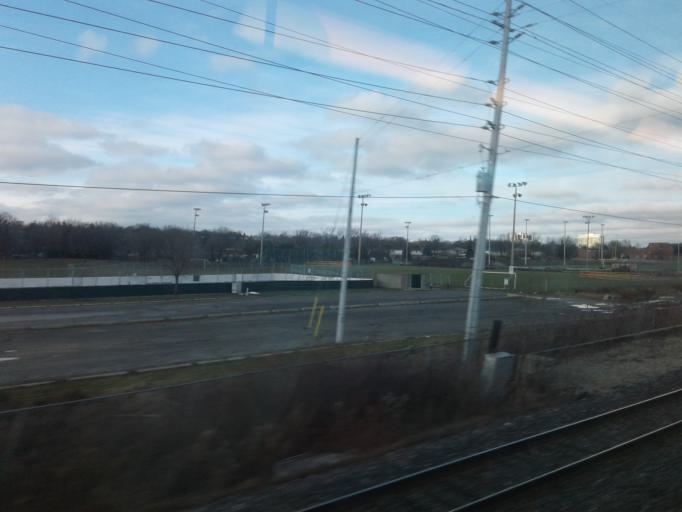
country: CA
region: Ontario
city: Oakville
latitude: 43.4993
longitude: -79.6466
